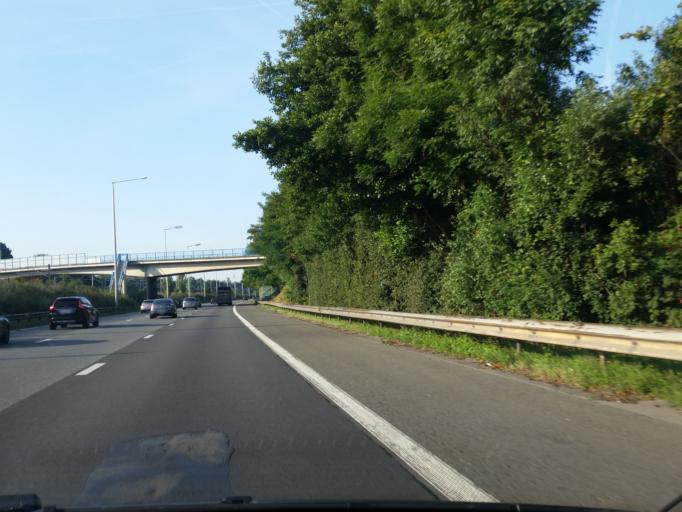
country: BE
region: Flanders
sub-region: Provincie Vlaams-Brabant
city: Zemst
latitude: 50.9655
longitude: 4.4904
